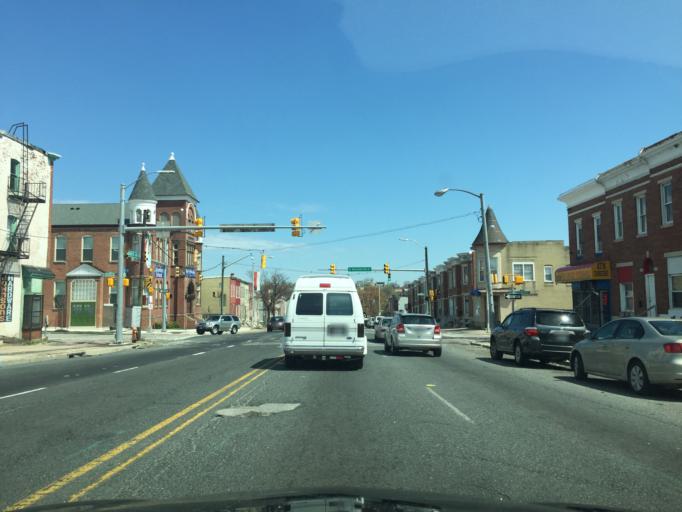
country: US
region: Maryland
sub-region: City of Baltimore
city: Baltimore
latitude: 39.3123
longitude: -76.5910
